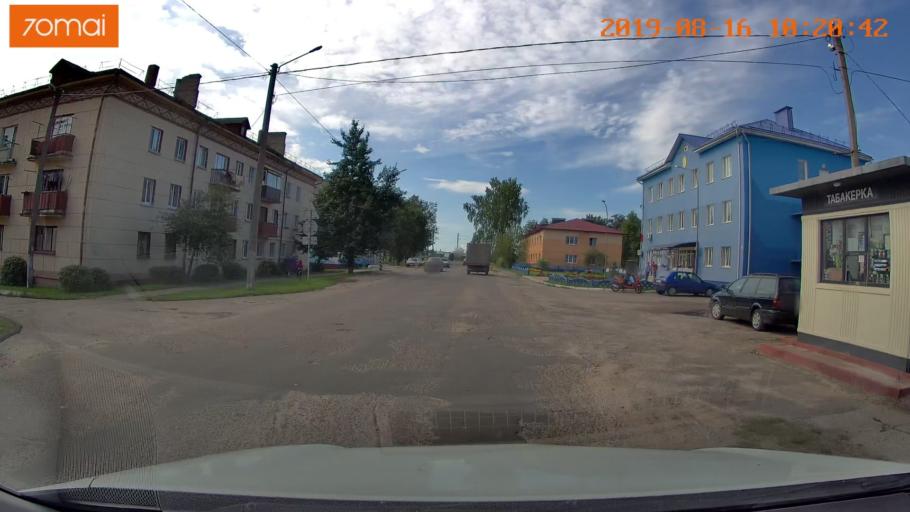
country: BY
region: Mogilev
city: Asipovichy
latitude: 53.2985
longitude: 28.6607
